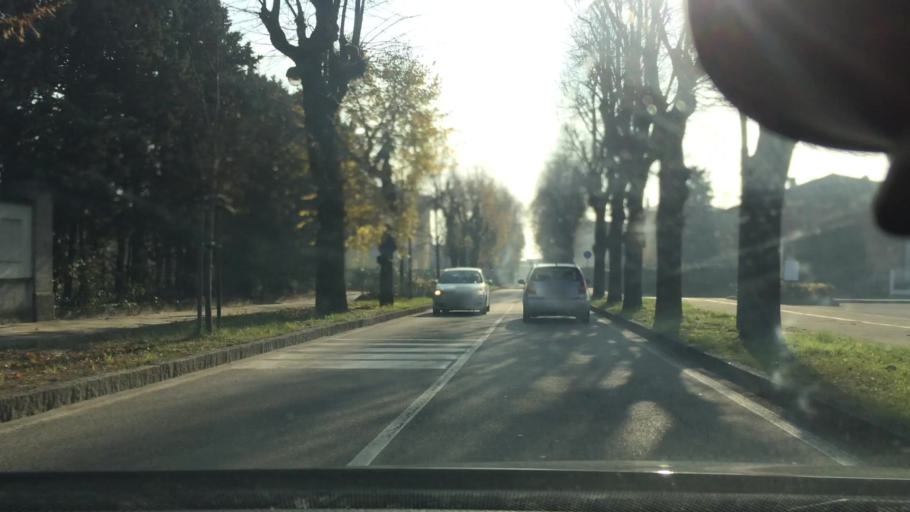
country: IT
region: Lombardy
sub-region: Citta metropolitana di Milano
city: Solaro
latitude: 45.6204
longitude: 9.0807
